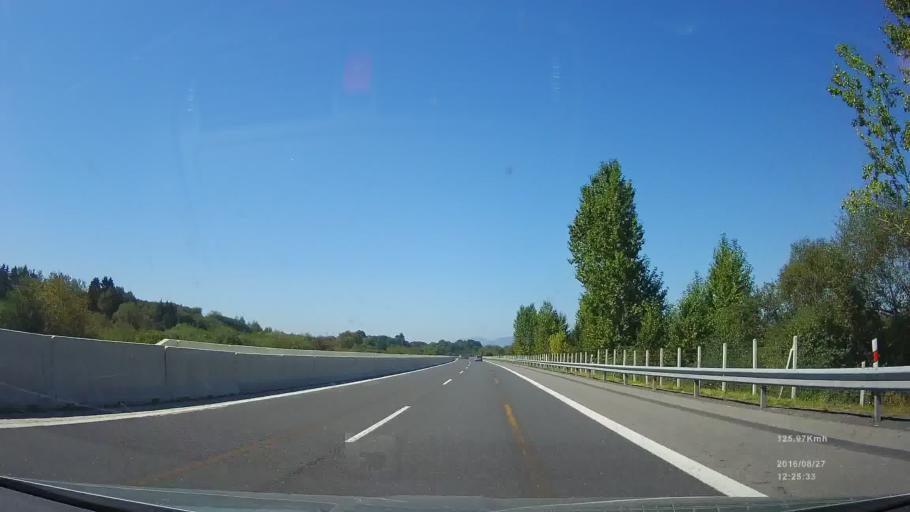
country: SK
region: Zilinsky
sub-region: Okres Liptovsky Mikulas
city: Liptovsky Mikulas
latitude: 49.0671
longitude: 19.6387
